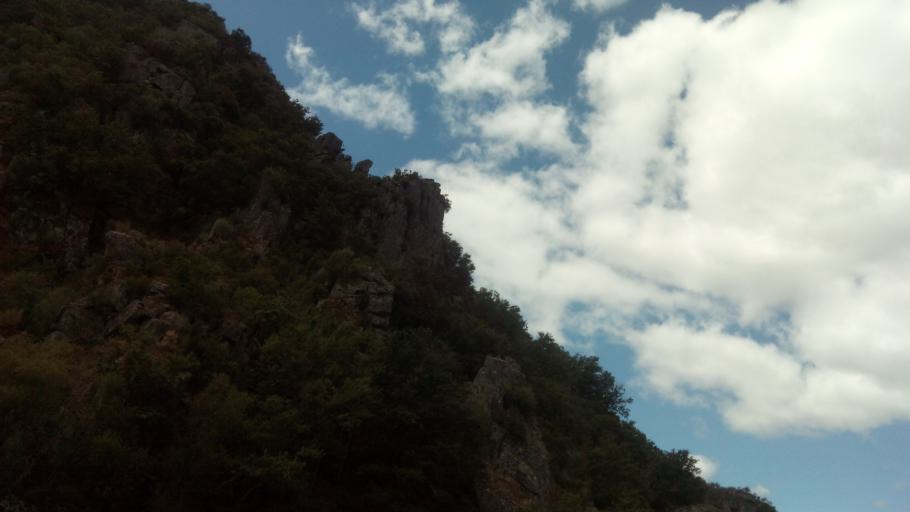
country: ES
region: Galicia
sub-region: Provincia de Lugo
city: Sober
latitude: 42.4057
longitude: -7.6316
